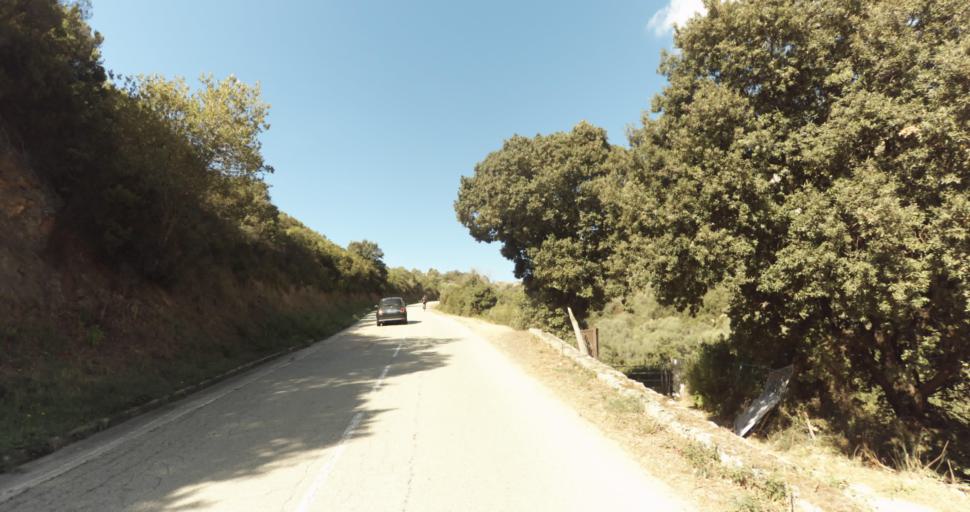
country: FR
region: Corsica
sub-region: Departement de la Corse-du-Sud
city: Ajaccio
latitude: 41.9338
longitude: 8.6833
